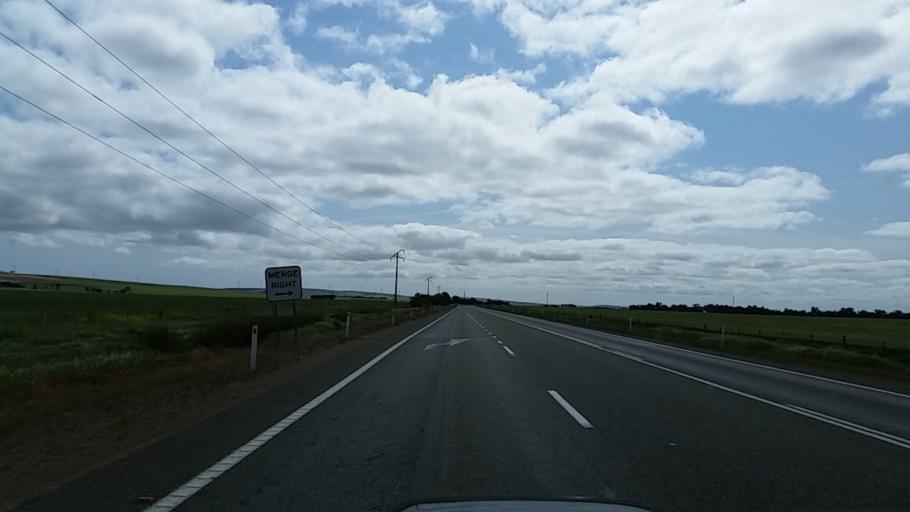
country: AU
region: South Australia
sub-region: Port Pirie City and Dists
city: Crystal Brook
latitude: -33.5236
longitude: 138.1989
